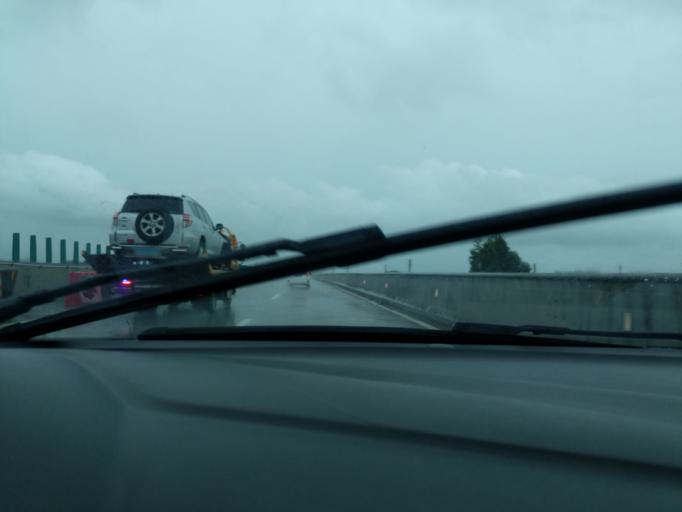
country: CN
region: Guangdong
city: Yueshan
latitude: 22.4637
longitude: 112.7410
